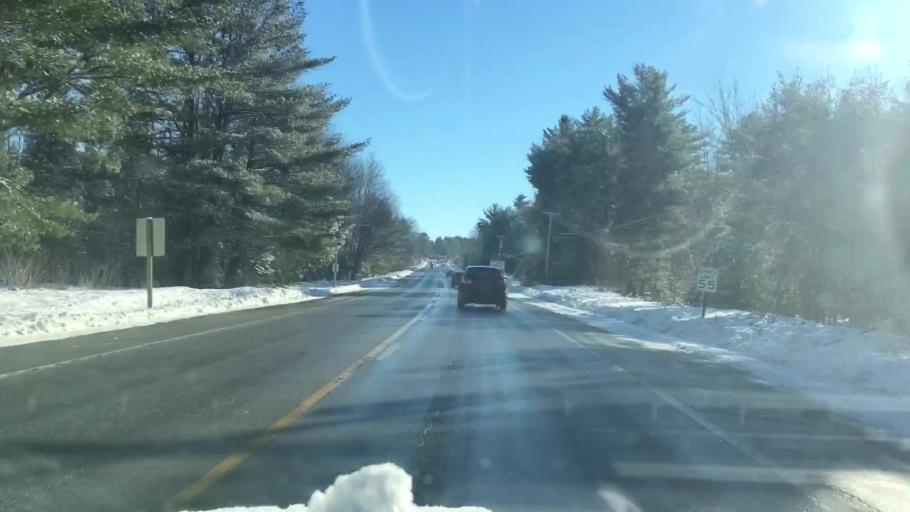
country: US
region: Maine
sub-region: Cumberland County
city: Bridgton
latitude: 44.0305
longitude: -70.6954
